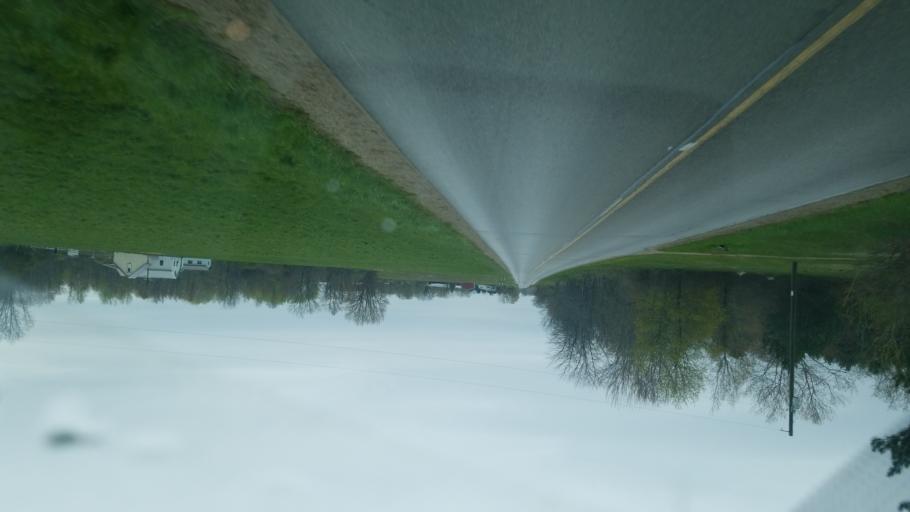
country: US
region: Michigan
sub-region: Montcalm County
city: Lakeview
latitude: 43.5020
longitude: -85.2541
